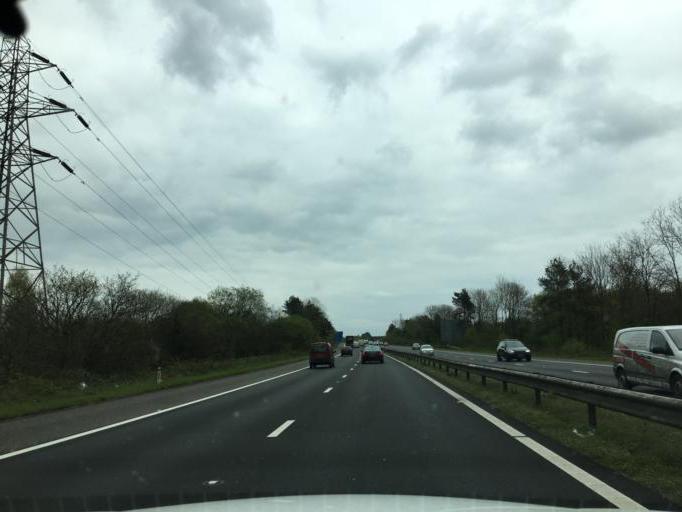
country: GB
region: Wales
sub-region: City and County of Swansea
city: Morriston
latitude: 51.6746
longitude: -3.9699
